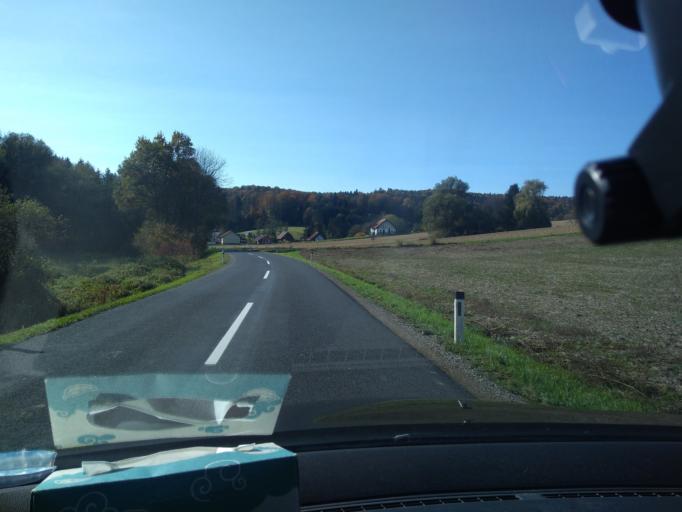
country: AT
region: Styria
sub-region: Politischer Bezirk Leibnitz
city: Sankt Ulrich am Waasen
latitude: 46.9086
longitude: 15.5295
